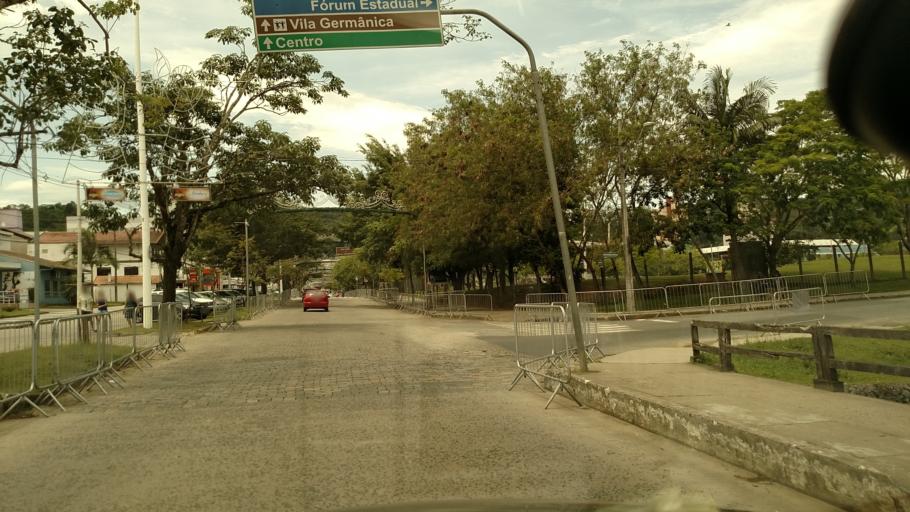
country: BR
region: Santa Catarina
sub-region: Blumenau
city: Blumenau
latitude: -26.9120
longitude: -49.0861
